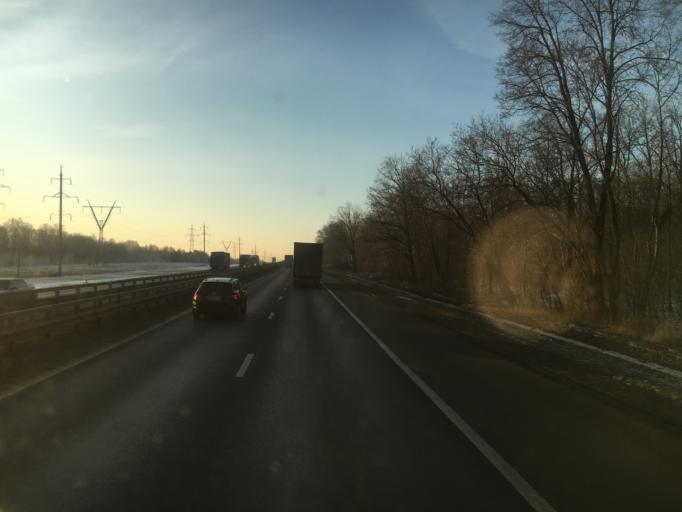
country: RU
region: Samara
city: Pribrezhnyy
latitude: 53.5187
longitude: 49.8153
